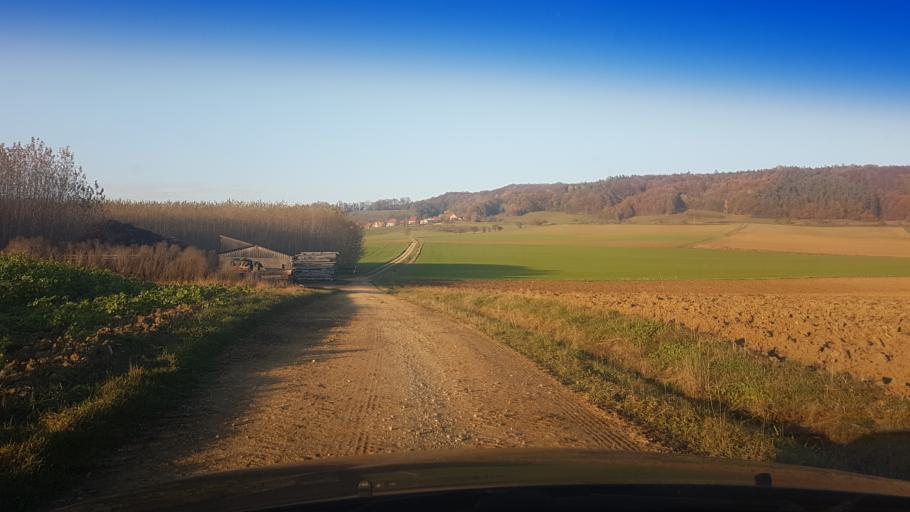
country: DE
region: Bavaria
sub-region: Upper Franconia
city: Schesslitz
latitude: 50.0061
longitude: 11.0233
